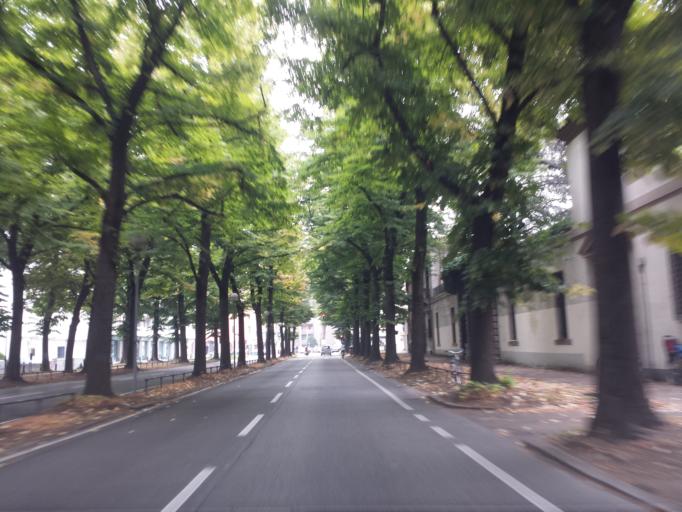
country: IT
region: Veneto
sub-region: Provincia di Padova
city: Padova
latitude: 45.4084
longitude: 11.8843
